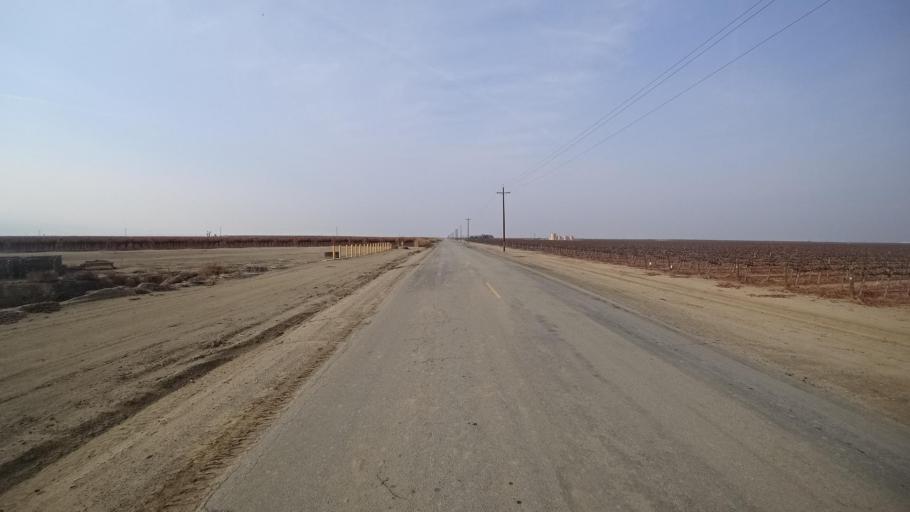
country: US
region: California
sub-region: Kern County
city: Greenfield
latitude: 35.0765
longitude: -119.0880
